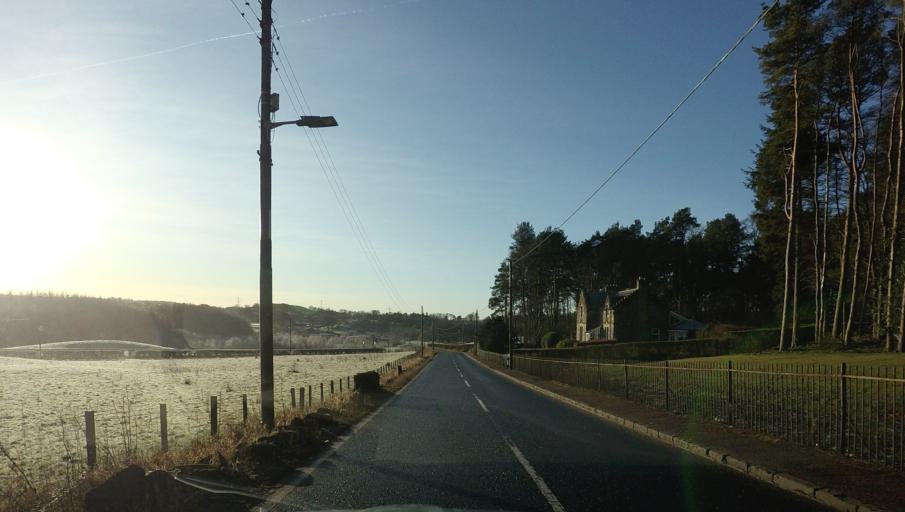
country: GB
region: Scotland
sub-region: North Lanarkshire
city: Shotts
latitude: 55.8081
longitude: -3.8378
